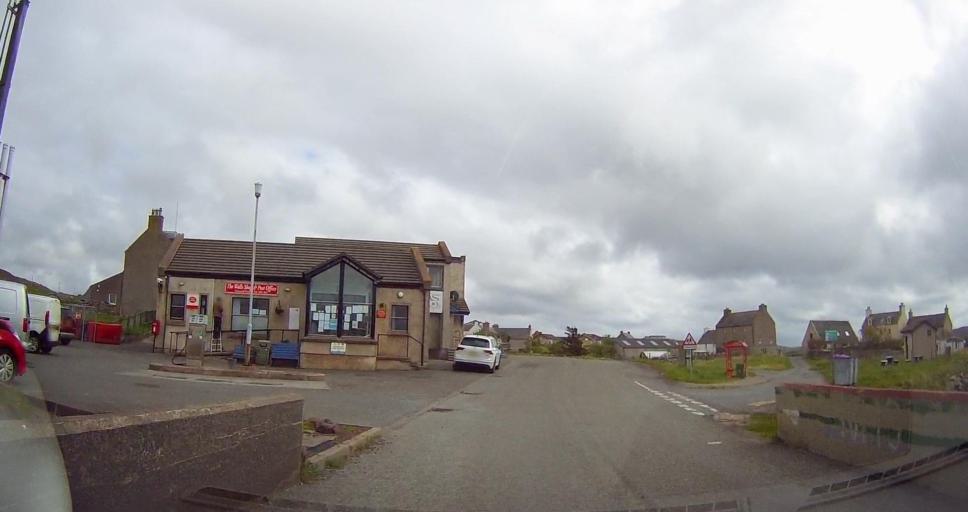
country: GB
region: Scotland
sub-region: Shetland Islands
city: Sandwick
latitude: 60.2289
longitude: -1.5639
